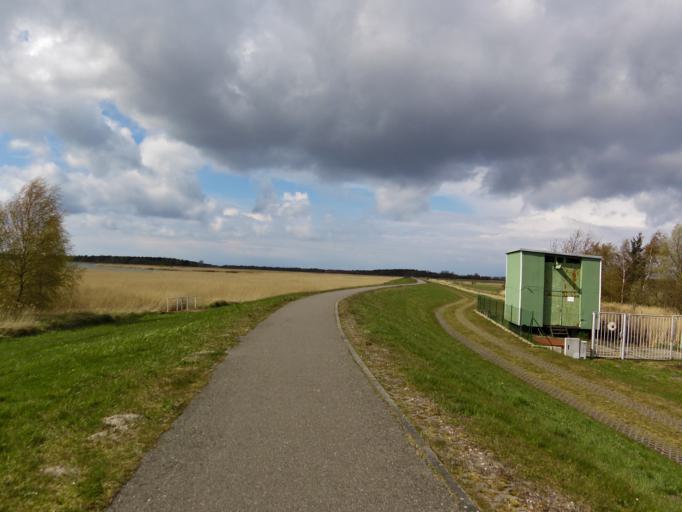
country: DE
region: Mecklenburg-Vorpommern
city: Zingst
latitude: 54.4247
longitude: 12.7296
